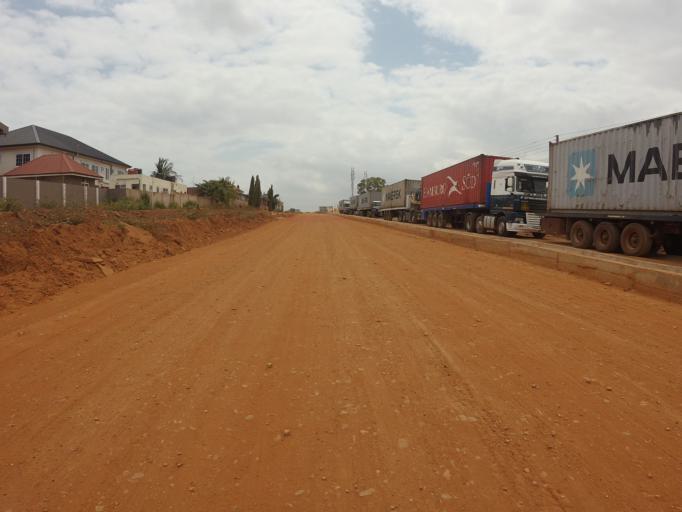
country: GH
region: Greater Accra
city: Medina Estates
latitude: 5.6285
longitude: -0.1444
